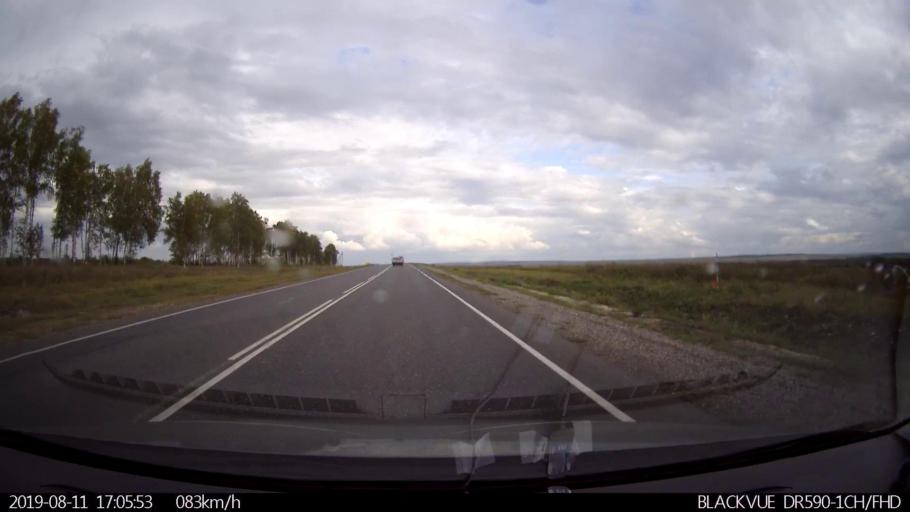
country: RU
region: Ulyanovsk
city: Mayna
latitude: 54.2964
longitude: 47.7952
